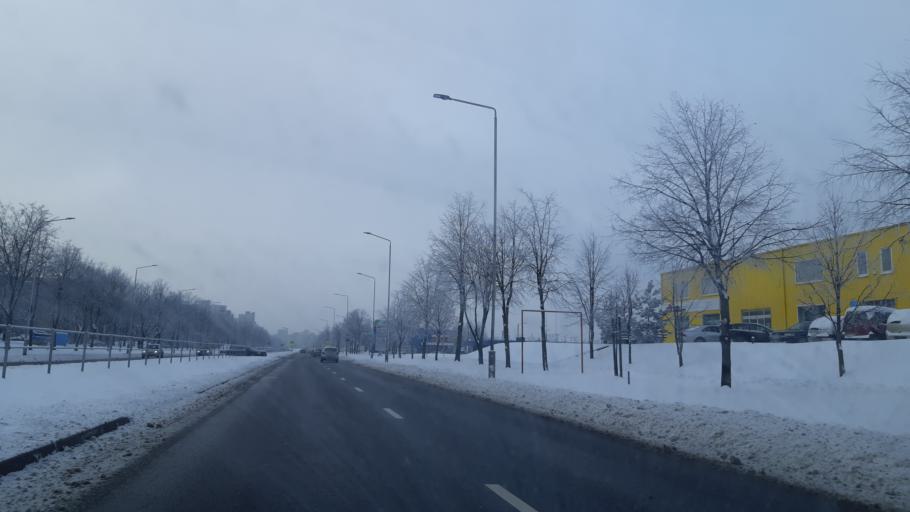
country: LT
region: Kauno apskritis
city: Dainava (Kaunas)
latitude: 54.9312
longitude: 23.9541
